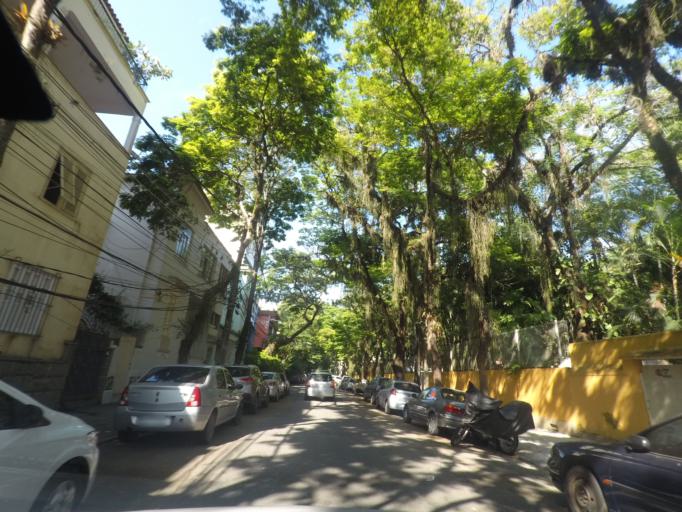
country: BR
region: Rio de Janeiro
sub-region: Rio De Janeiro
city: Rio de Janeiro
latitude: -22.9722
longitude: -43.2249
